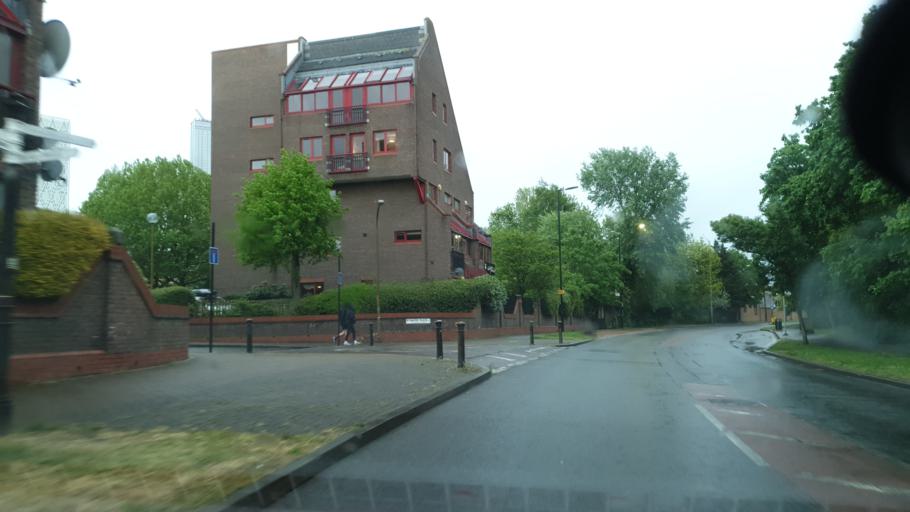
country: GB
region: England
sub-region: Greater London
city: Poplar
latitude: 51.5051
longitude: -0.0369
